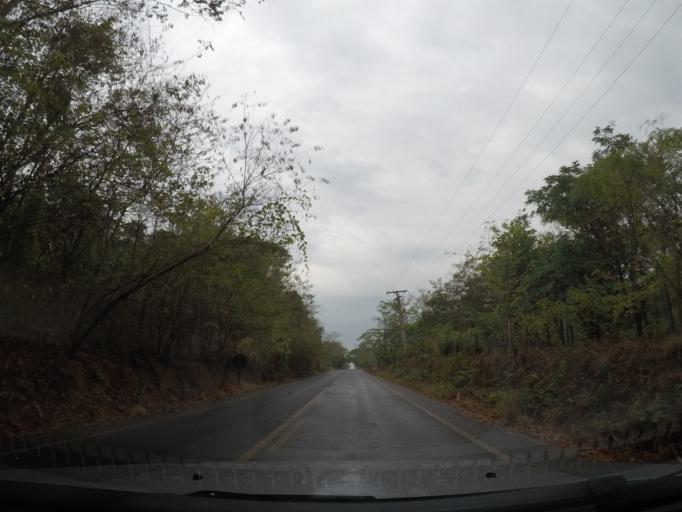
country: BR
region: Goias
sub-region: Pirenopolis
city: Pirenopolis
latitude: -15.8491
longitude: -48.9284
